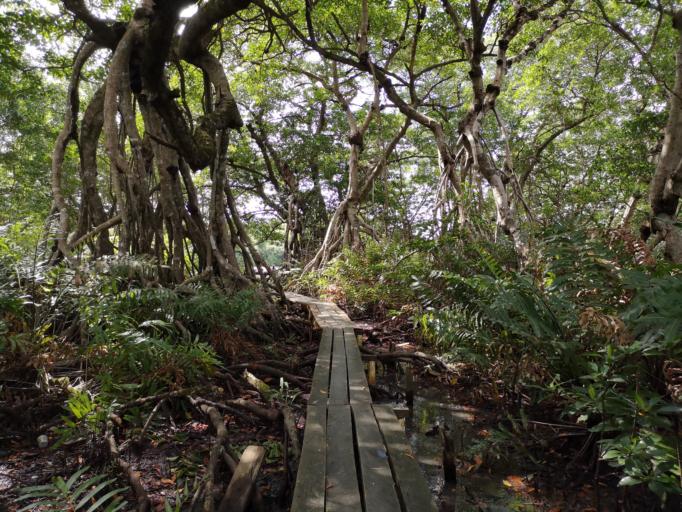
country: CO
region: Antioquia
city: Turbo
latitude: 8.0889
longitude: -76.8368
